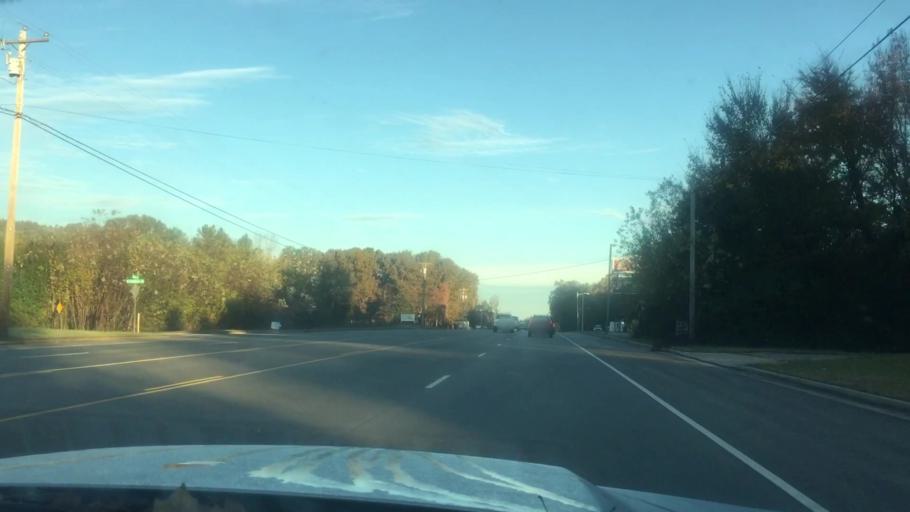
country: US
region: Tennessee
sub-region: Franklin County
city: Estill Springs
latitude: 35.2866
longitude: -86.1423
